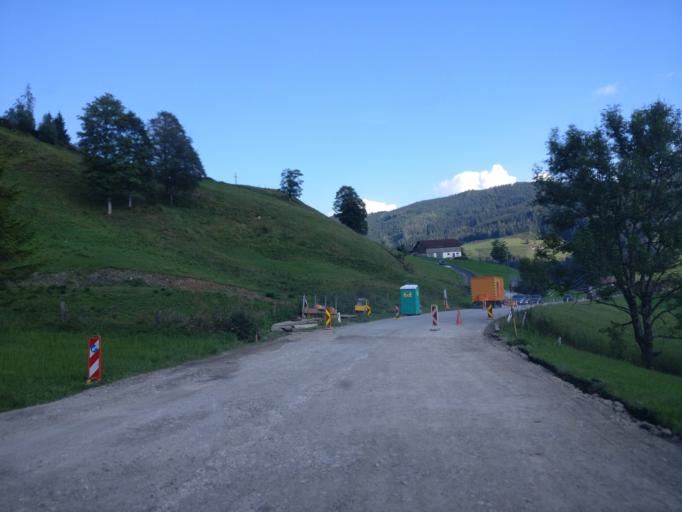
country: AT
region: Salzburg
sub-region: Politischer Bezirk Sankt Johann im Pongau
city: Muhlbach am Hochkonig
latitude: 47.3830
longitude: 13.1252
